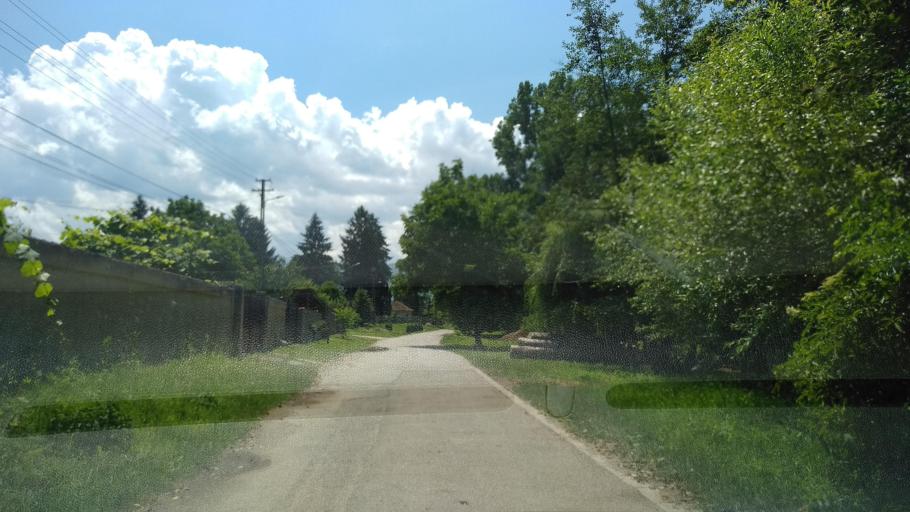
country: RO
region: Hunedoara
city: Densus
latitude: 45.5459
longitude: 22.8207
